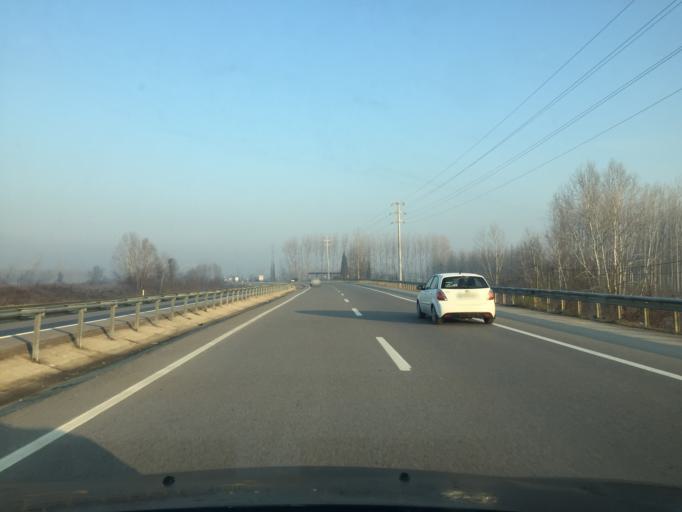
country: TR
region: Sakarya
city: Akyazi
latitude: 40.6919
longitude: 30.5734
